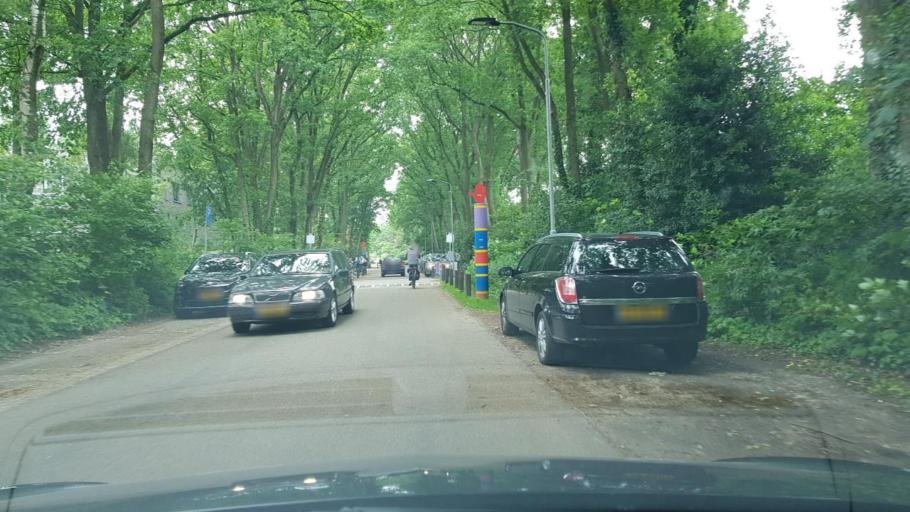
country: NL
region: Gelderland
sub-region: Gemeente Ermelo
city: Ermelo
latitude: 52.2945
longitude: 5.6374
